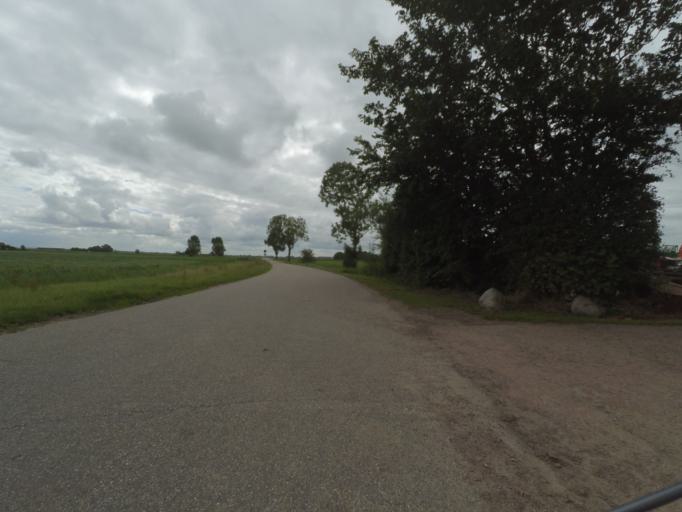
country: NL
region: Friesland
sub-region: Gemeente Dongeradeel
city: Anjum
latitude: 53.3222
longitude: 6.1017
